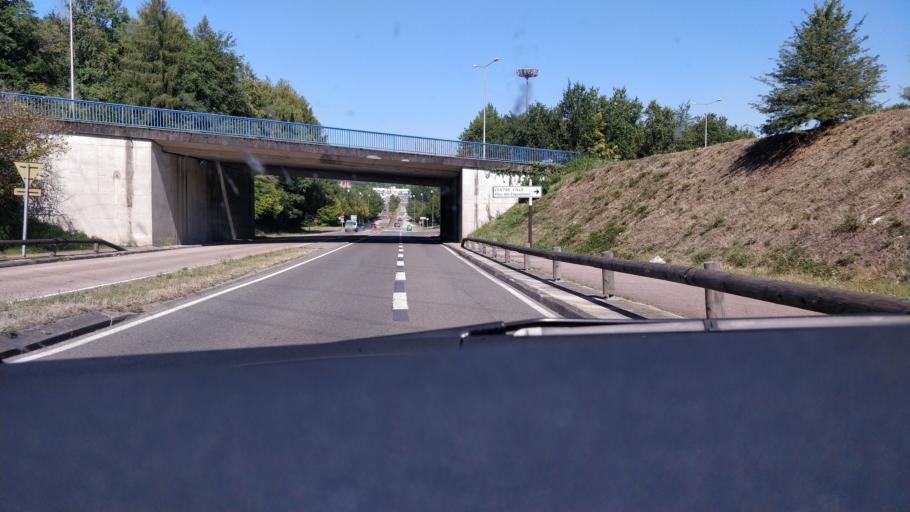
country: FR
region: Limousin
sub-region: Departement de la Haute-Vienne
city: Limoges
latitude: 45.8622
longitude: 1.2744
